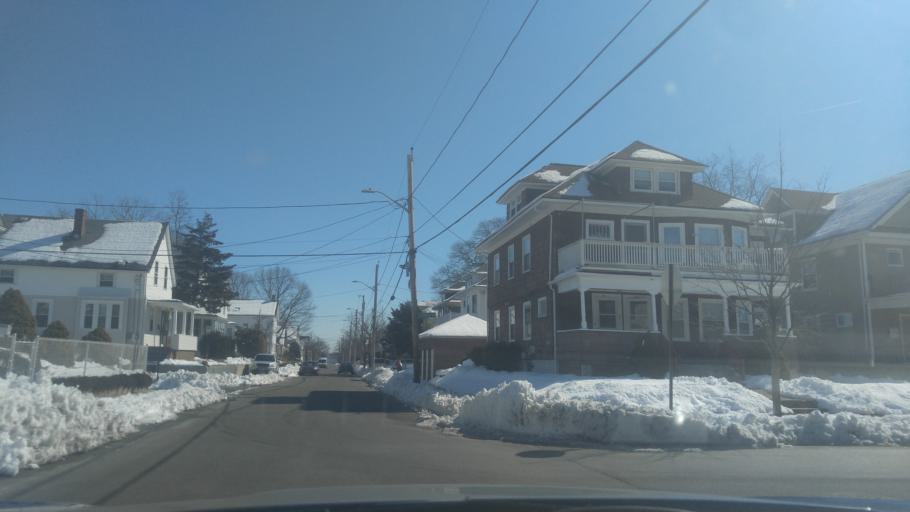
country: US
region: Rhode Island
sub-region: Providence County
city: Cranston
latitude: 41.7838
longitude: -71.3980
